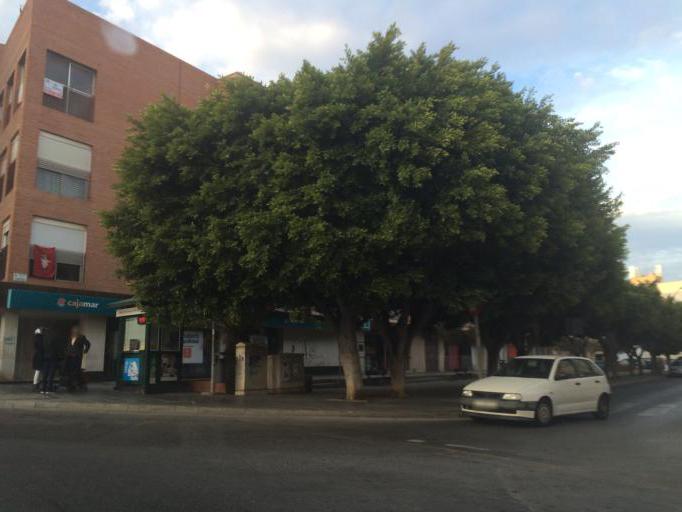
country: ES
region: Andalusia
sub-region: Provincia de Almeria
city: Almeria
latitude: 36.8463
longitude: -2.4669
